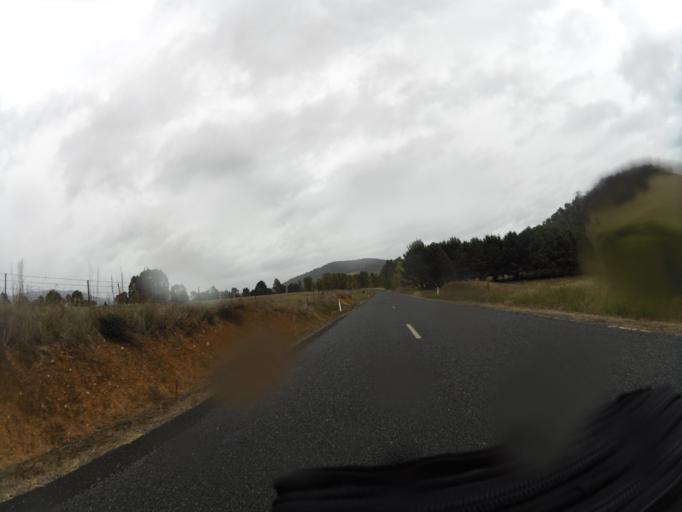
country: AU
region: New South Wales
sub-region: Greater Hume Shire
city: Holbrook
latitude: -36.2311
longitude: 147.6545
